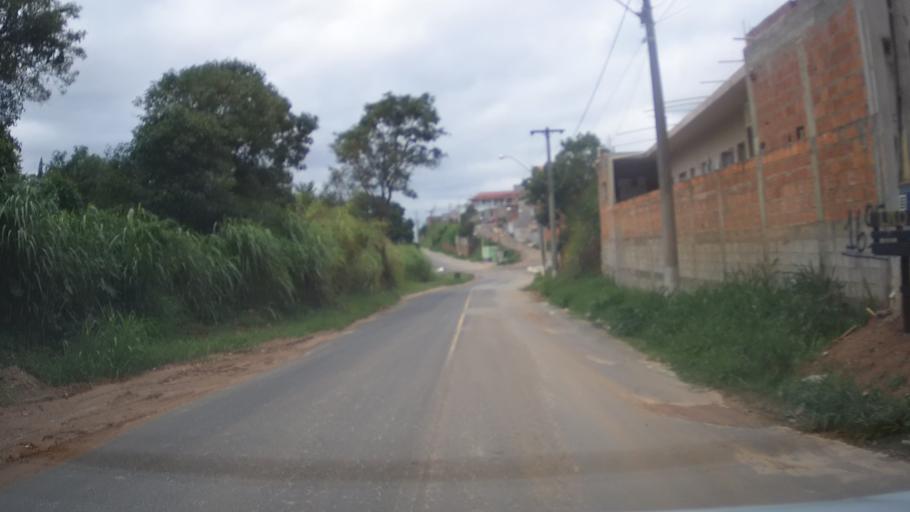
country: BR
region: Sao Paulo
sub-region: Louveira
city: Louveira
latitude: -23.0976
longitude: -46.9988
